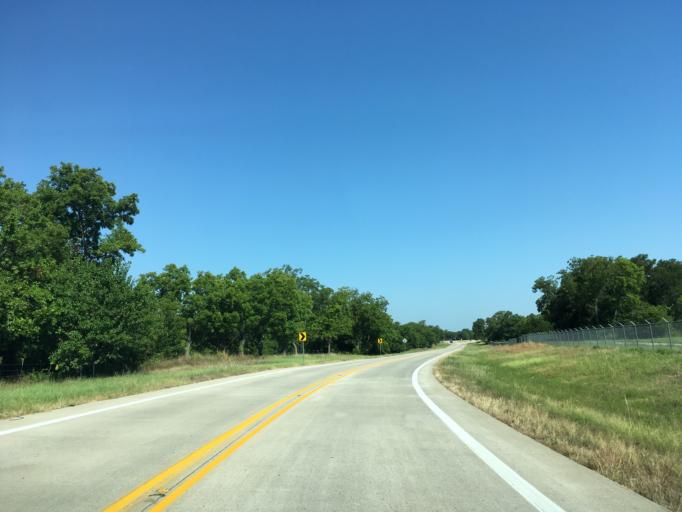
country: US
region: Texas
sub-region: Collin County
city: Fairview
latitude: 33.1605
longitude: -96.5911
